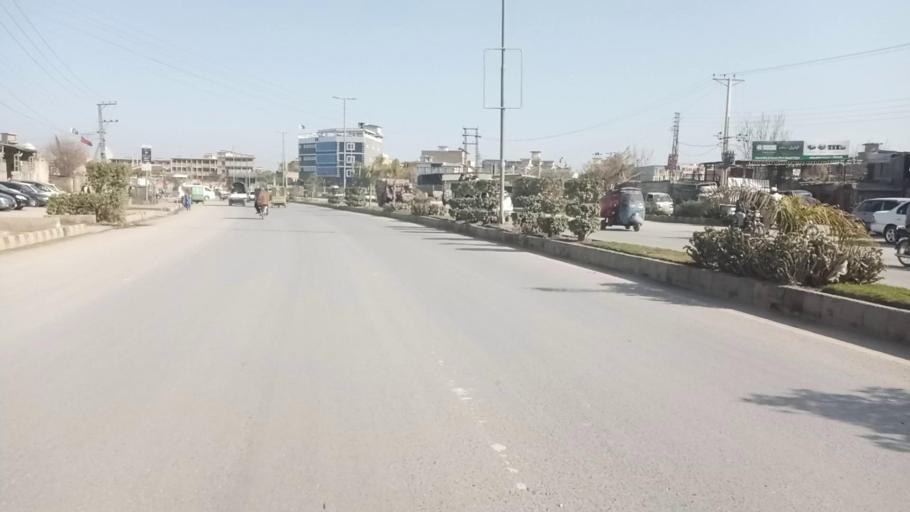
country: PK
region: Khyber Pakhtunkhwa
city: Peshawar
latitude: 34.0307
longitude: 71.5936
